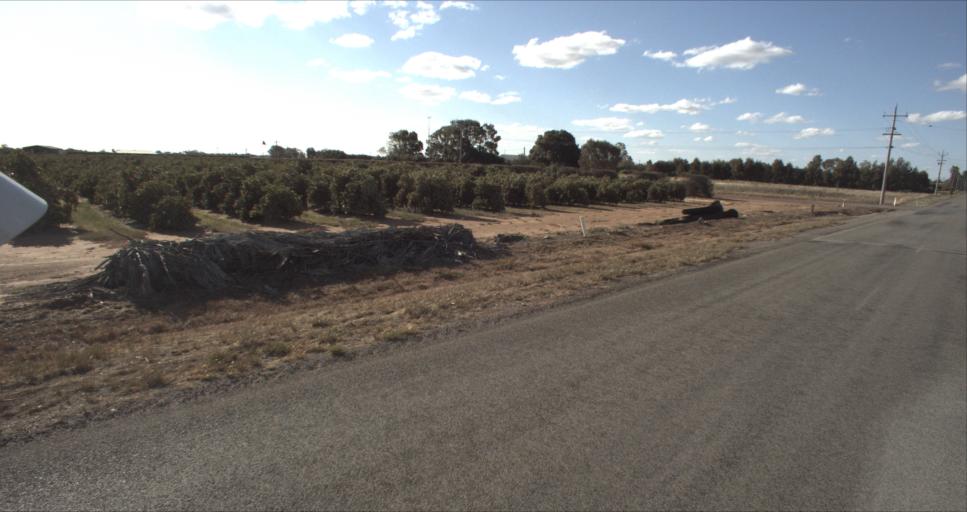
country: AU
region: New South Wales
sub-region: Leeton
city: Leeton
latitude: -34.5286
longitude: 146.2819
